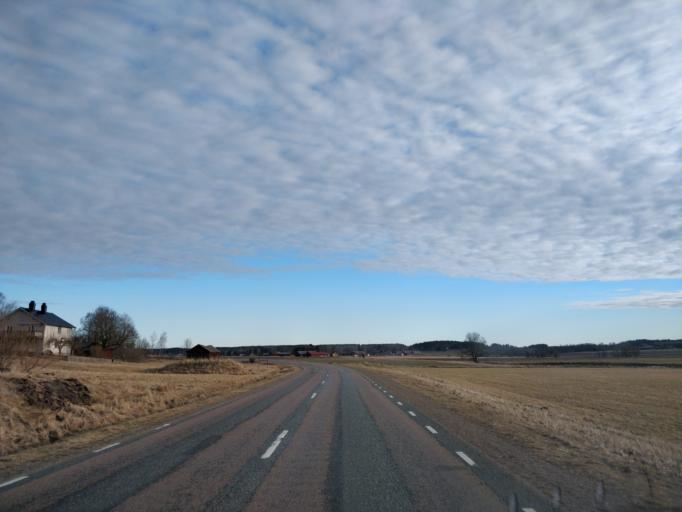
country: SE
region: Uppsala
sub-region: Enkopings Kommun
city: Enkoping
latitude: 59.7916
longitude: 17.0887
